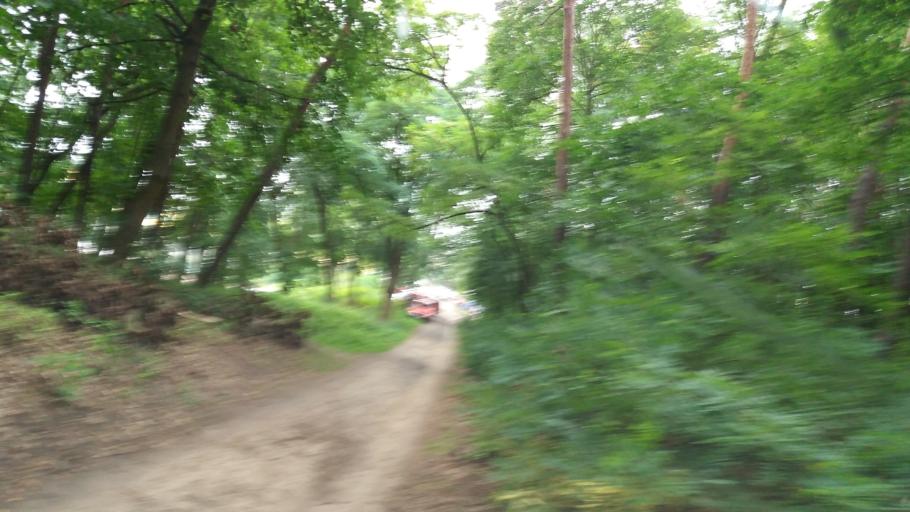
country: PL
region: West Pomeranian Voivodeship
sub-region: Powiat mysliborski
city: Barlinek
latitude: 52.9963
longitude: 15.2283
